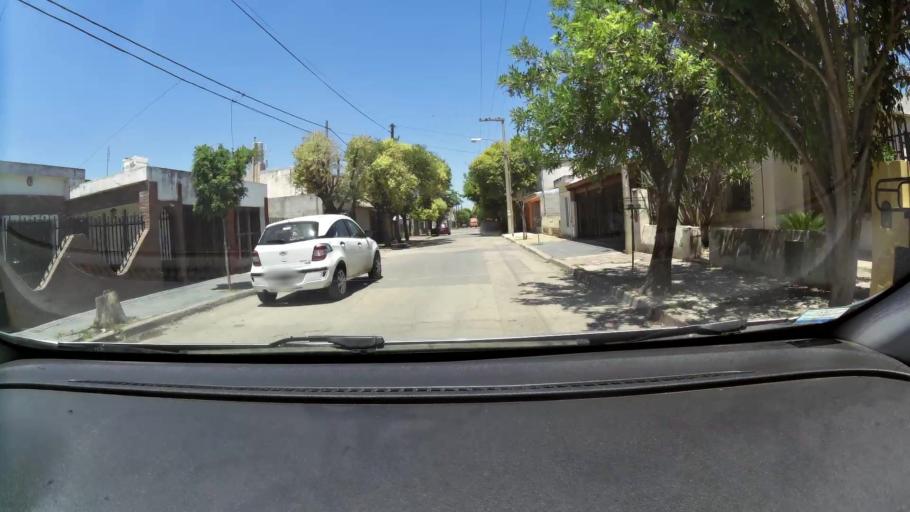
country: AR
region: Cordoba
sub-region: Departamento de Capital
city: Cordoba
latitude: -31.3786
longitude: -64.1325
